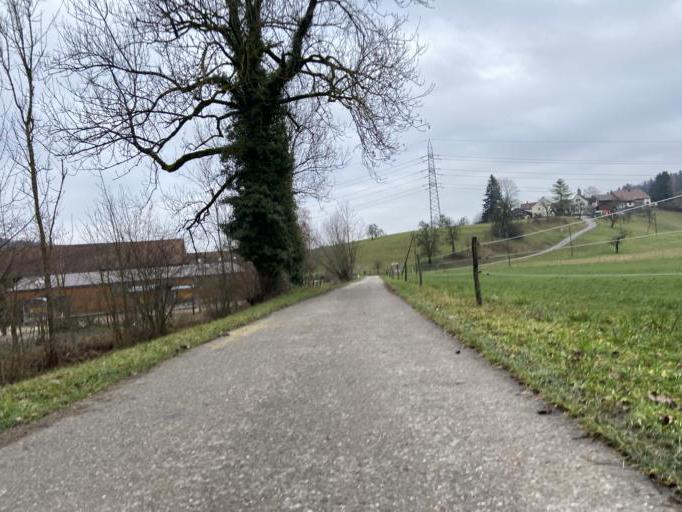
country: CH
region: Zurich
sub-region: Bezirk Winterthur
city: Wuelflingen (Kreis 6) / Niederfeld
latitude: 47.4940
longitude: 8.6739
